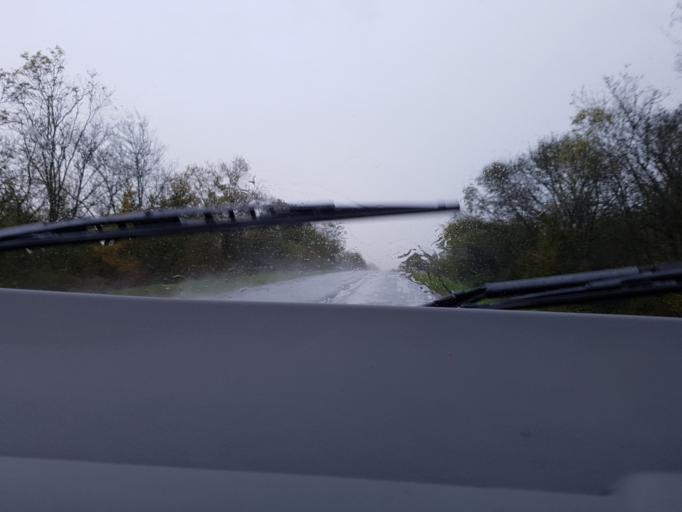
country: FR
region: Aquitaine
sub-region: Departement de la Gironde
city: Saint-Louis-de-Montferrand
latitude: 44.9363
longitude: -0.5250
